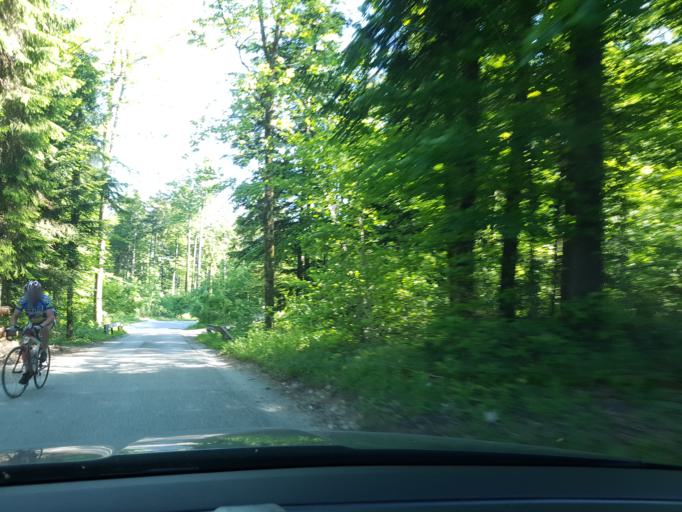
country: AT
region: Salzburg
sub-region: Politischer Bezirk Salzburg-Umgebung
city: Koppl
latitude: 47.7857
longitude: 13.1243
